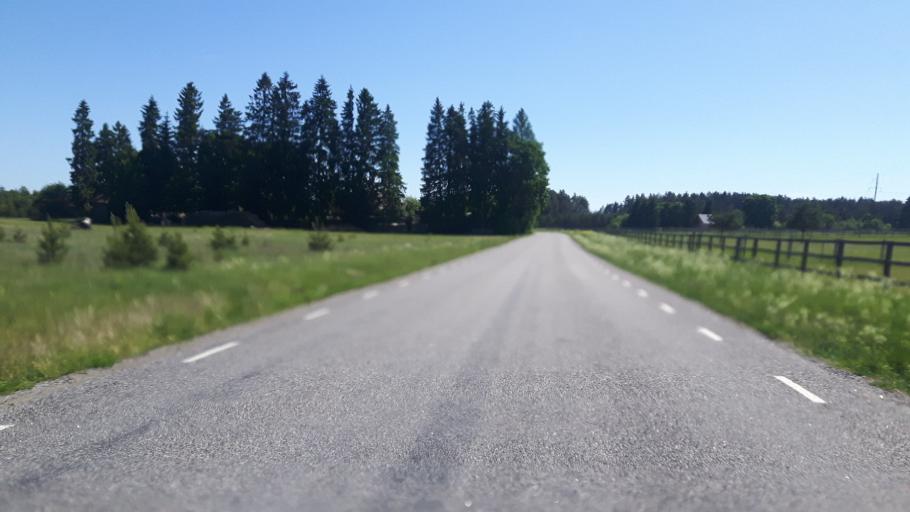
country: EE
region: Raplamaa
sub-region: Kohila vald
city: Kohila
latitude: 59.1963
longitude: 24.6977
